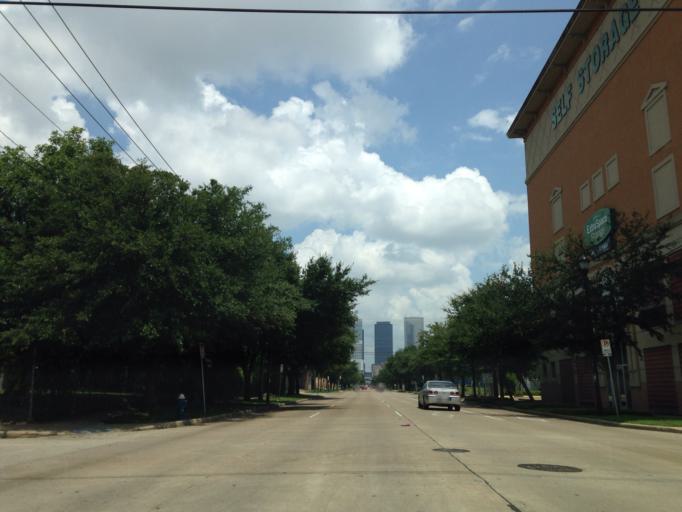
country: US
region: Texas
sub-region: Harris County
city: Houston
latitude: 29.7410
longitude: -95.3750
